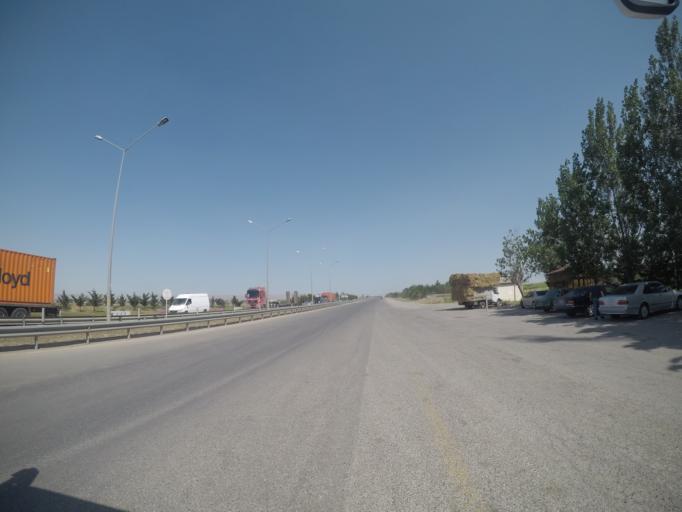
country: AZ
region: Haciqabul
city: Haciqabul
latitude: 40.0330
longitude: 49.0896
